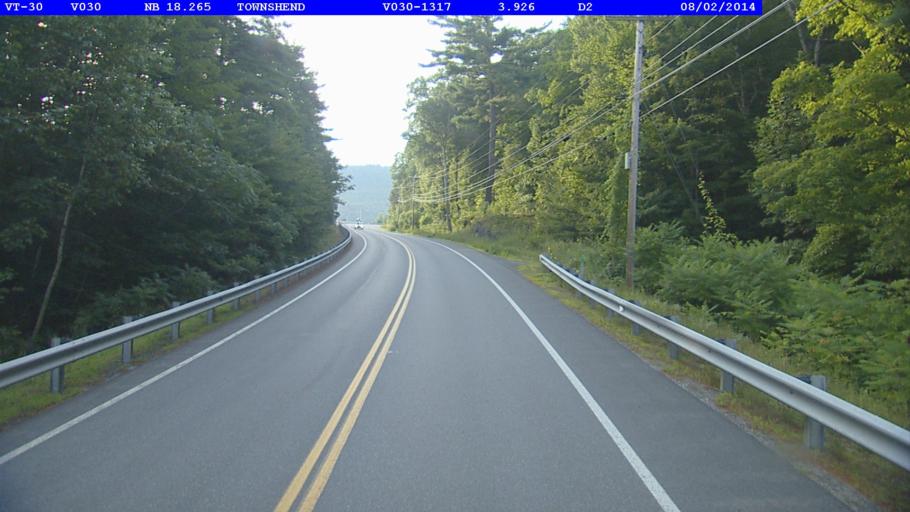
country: US
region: Vermont
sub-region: Windham County
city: Newfane
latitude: 43.0527
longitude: -72.6986
